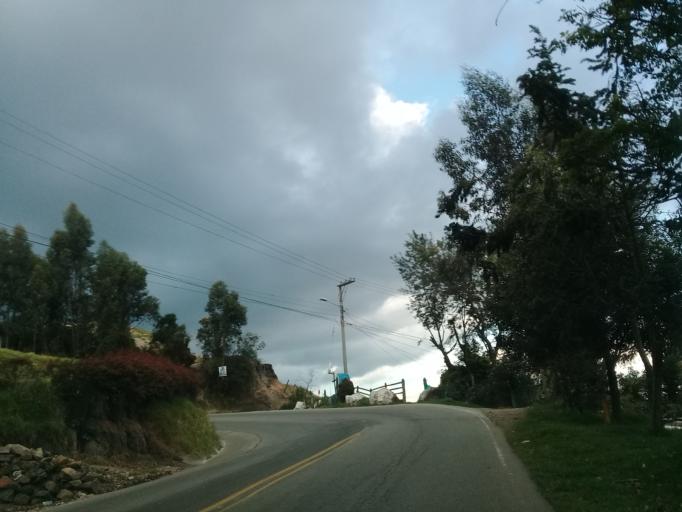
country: CO
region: Cundinamarca
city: Zipaquira
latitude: 5.0274
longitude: -74.0227
